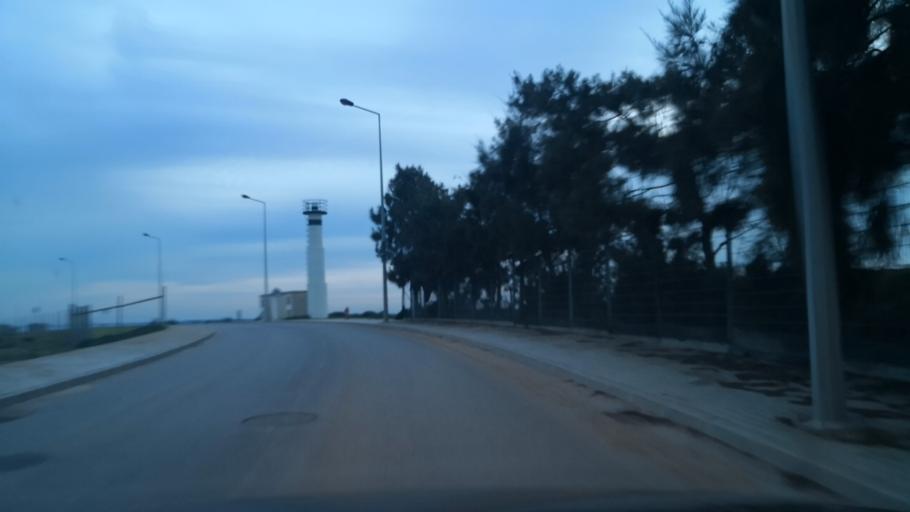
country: PT
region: Setubal
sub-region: Setubal
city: Setubal
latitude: 38.5035
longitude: -8.8389
